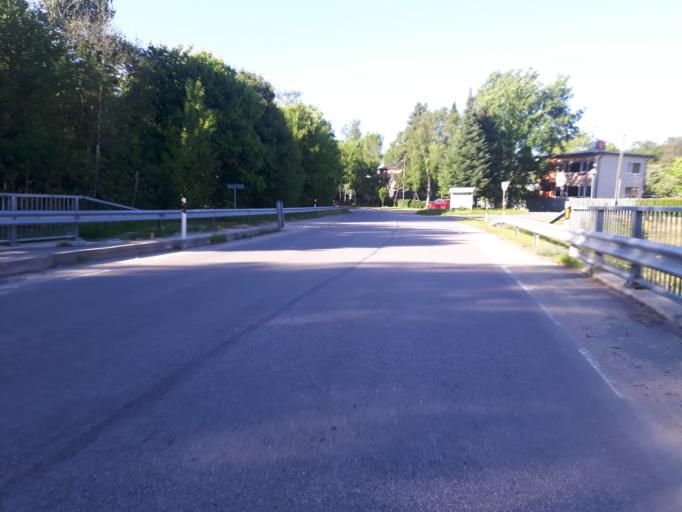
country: EE
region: Harju
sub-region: Loksa linn
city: Loksa
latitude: 59.5724
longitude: 25.9701
